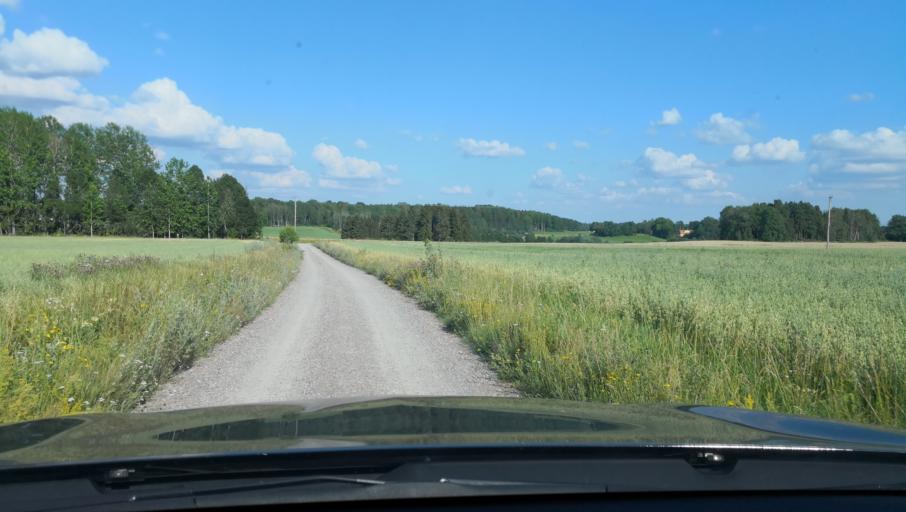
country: SE
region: Vaestmanland
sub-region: Vasteras
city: Skultuna
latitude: 59.7085
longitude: 16.4093
